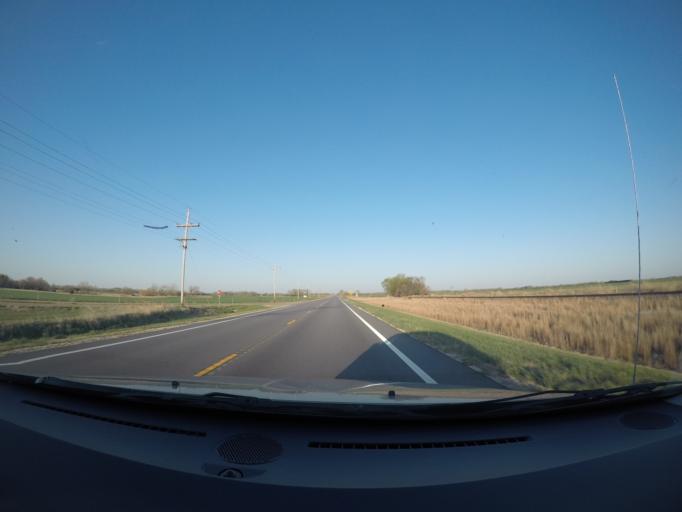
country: US
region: Kansas
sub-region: Stafford County
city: Stafford
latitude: 37.8395
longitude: -98.3589
